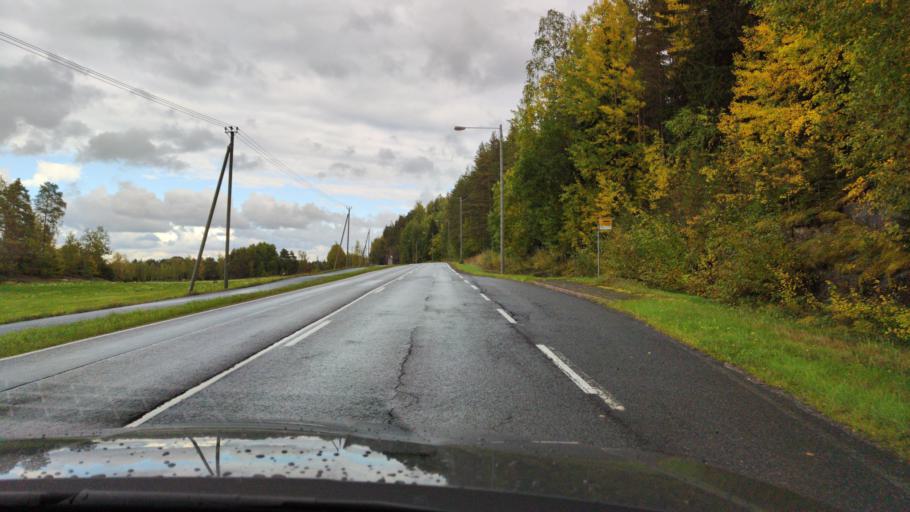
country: FI
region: Varsinais-Suomi
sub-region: Turku
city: Turku
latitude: 60.3642
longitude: 22.1974
